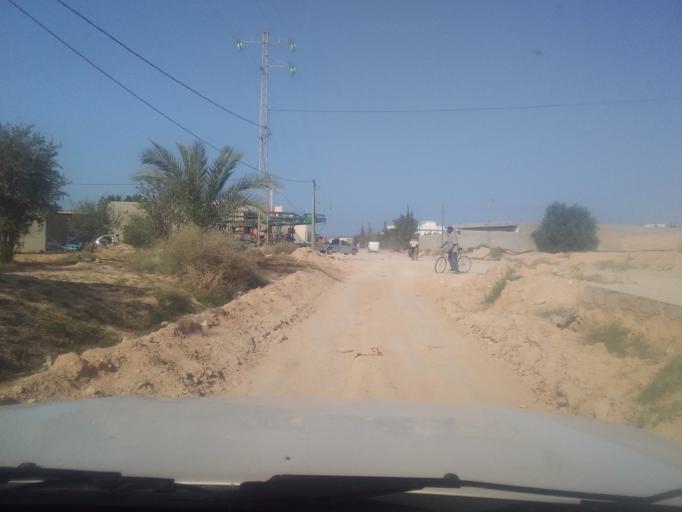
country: TN
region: Qabis
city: Matmata
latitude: 33.6084
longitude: 10.2809
